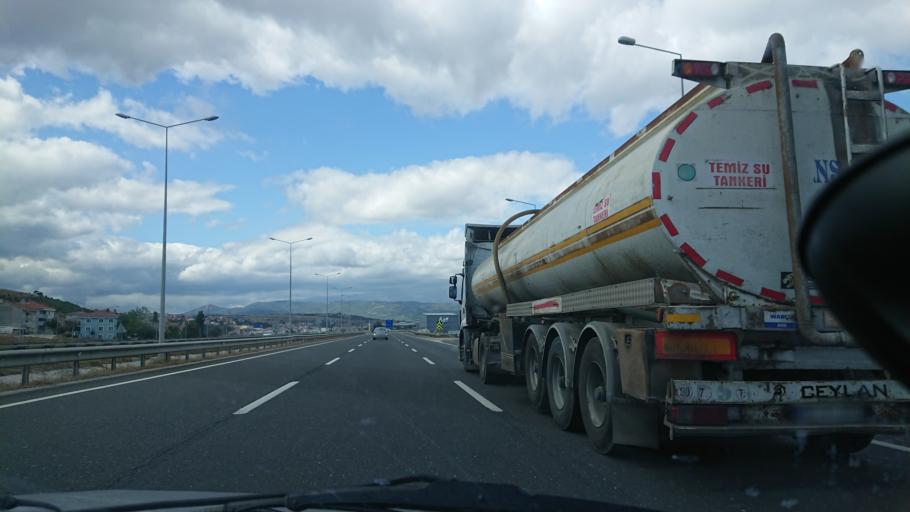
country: TR
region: Bilecik
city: Bozuyuk
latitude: 39.8961
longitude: 30.0562
